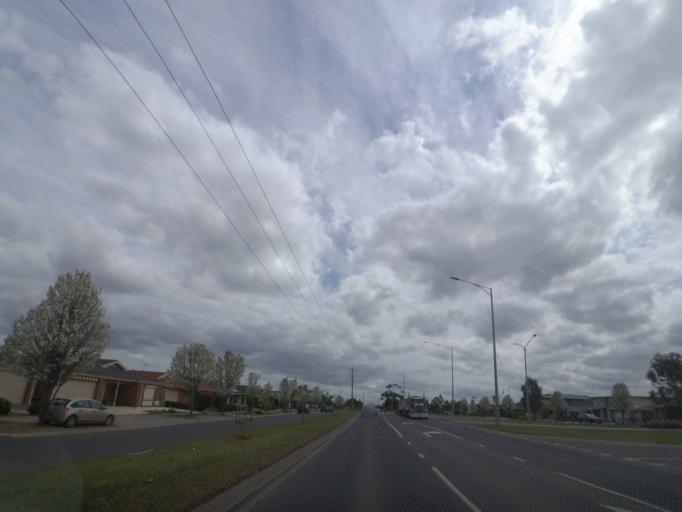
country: AU
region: Victoria
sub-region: Wyndham
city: Tarneit
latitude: -37.8458
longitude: 144.6635
